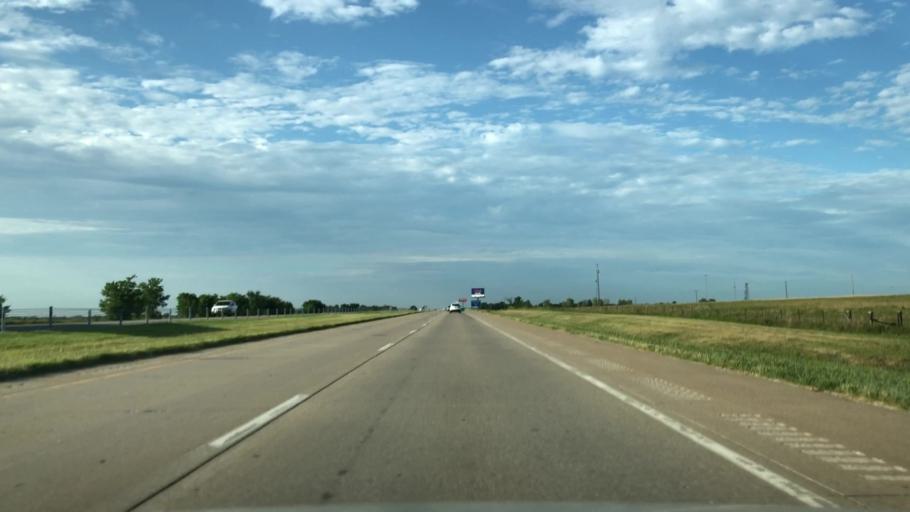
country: US
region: Oklahoma
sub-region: Osage County
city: Skiatook
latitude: 36.3762
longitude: -95.9207
